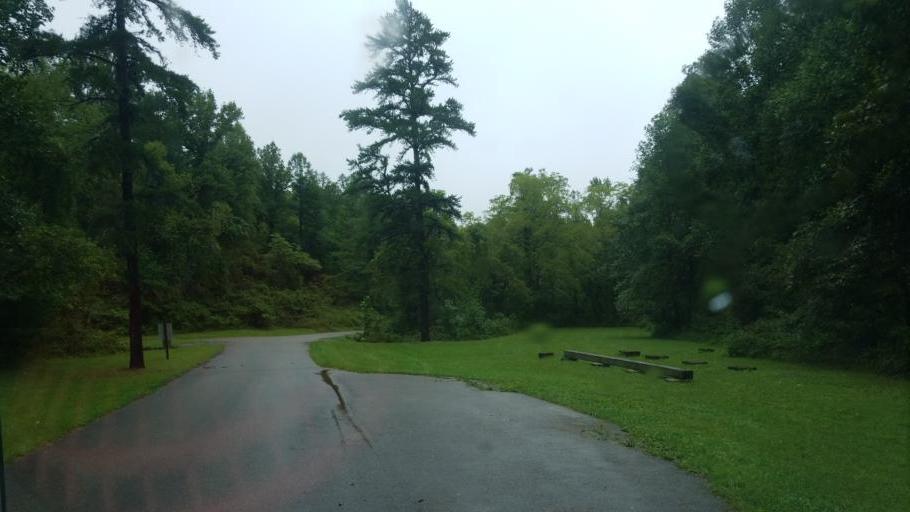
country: US
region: Ohio
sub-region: Scioto County
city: West Portsmouth
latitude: 38.7744
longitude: -83.1390
